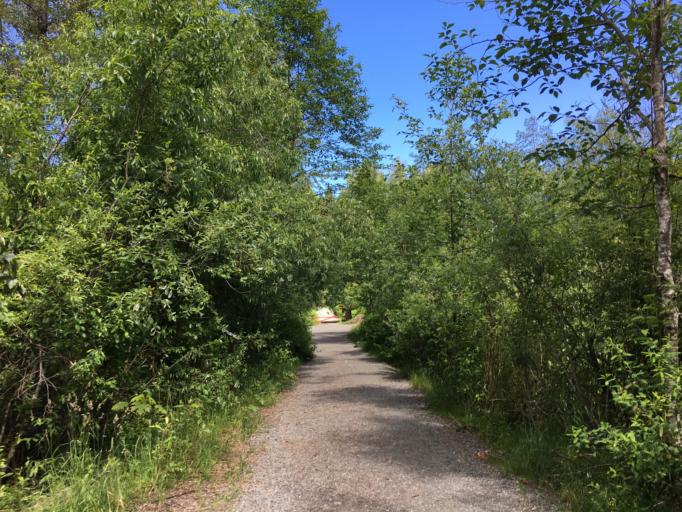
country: CA
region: British Columbia
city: Cumberland
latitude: 49.6159
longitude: -125.0494
